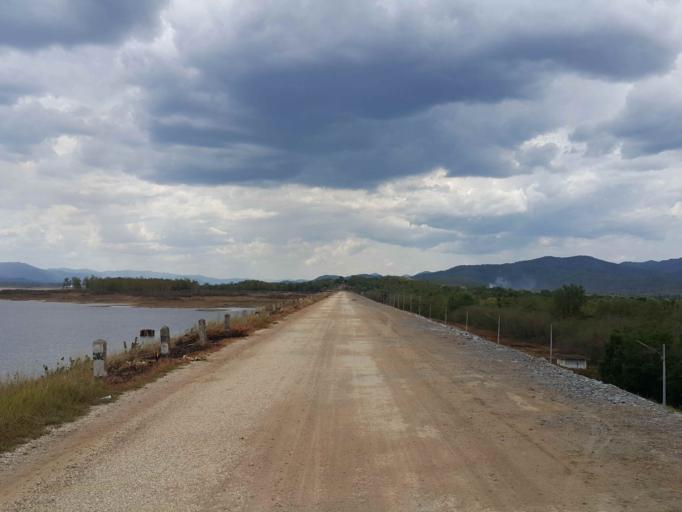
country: TH
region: Sukhothai
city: Thung Saliam
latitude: 17.3142
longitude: 99.4249
